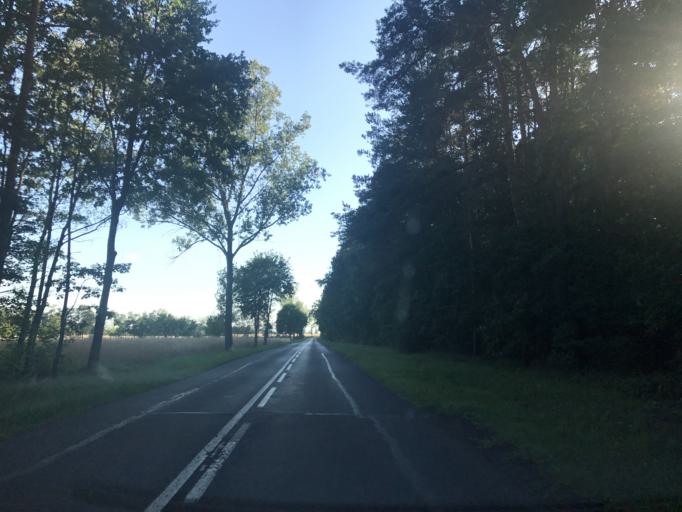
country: PL
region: Greater Poland Voivodeship
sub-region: Powiat koninski
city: Rychwal
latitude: 52.0856
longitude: 18.2165
